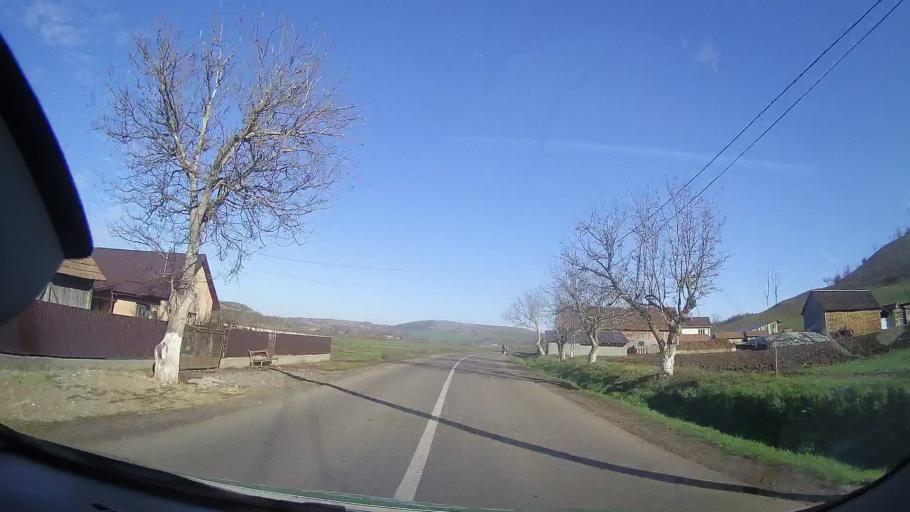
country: RO
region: Mures
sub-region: Comuna Band
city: Band
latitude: 46.5745
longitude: 24.3478
